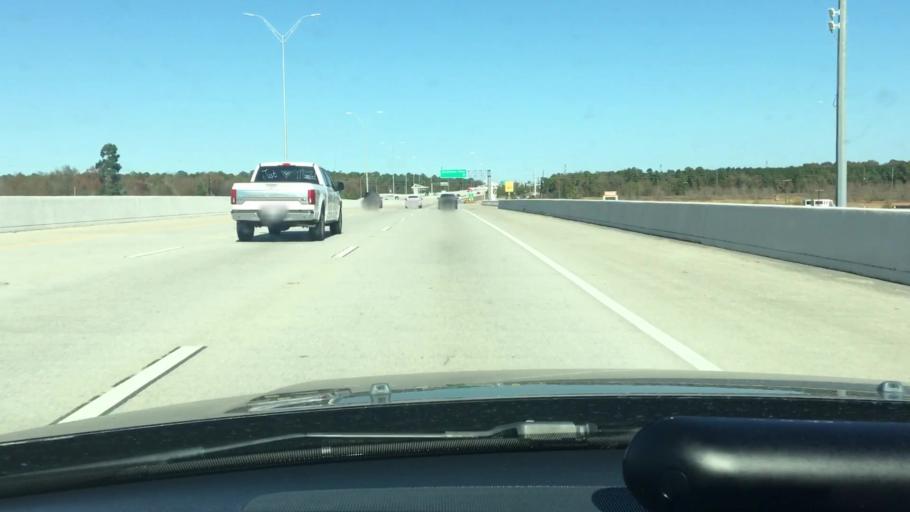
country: US
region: Texas
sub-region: Harris County
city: Sheldon
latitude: 29.8966
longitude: -95.2030
